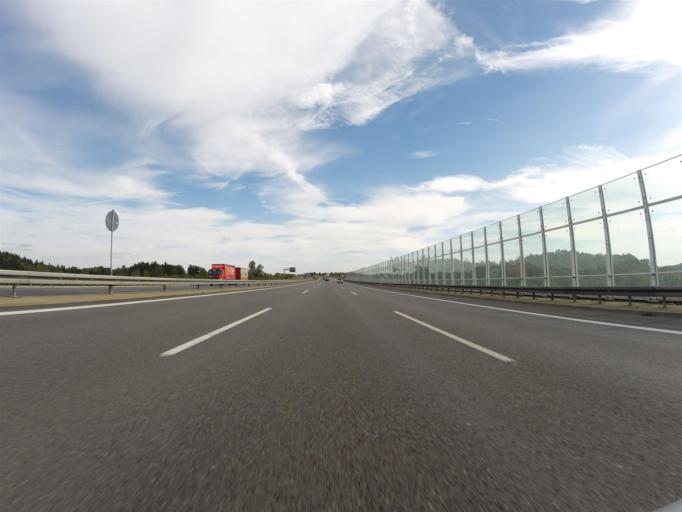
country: DE
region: Saxony
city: Nossen
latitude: 51.0372
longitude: 13.3164
